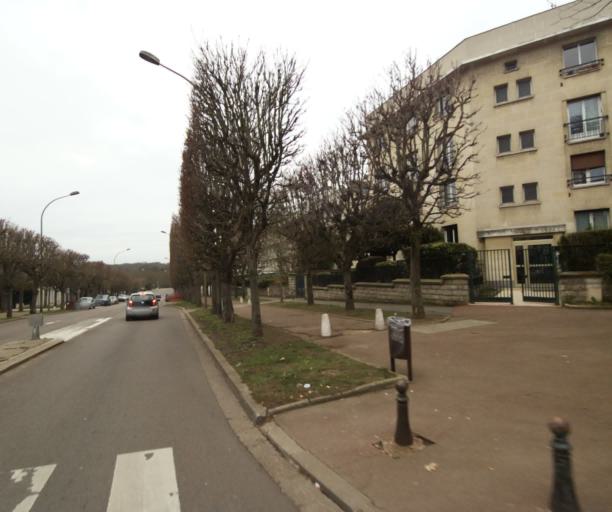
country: FR
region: Ile-de-France
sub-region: Departement des Hauts-de-Seine
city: Saint-Cloud
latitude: 48.8421
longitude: 2.2070
